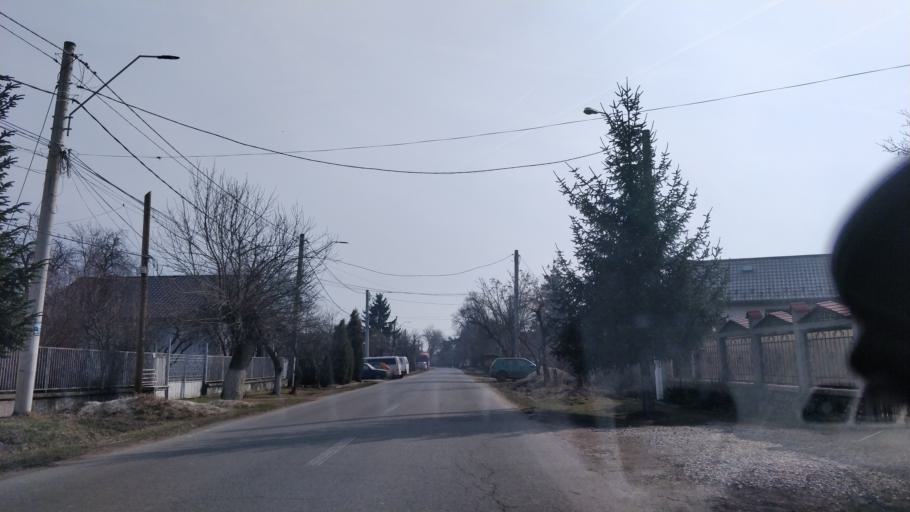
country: RO
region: Giurgiu
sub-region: Comuna Ulmi
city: Ulmi
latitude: 44.4665
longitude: 25.7726
